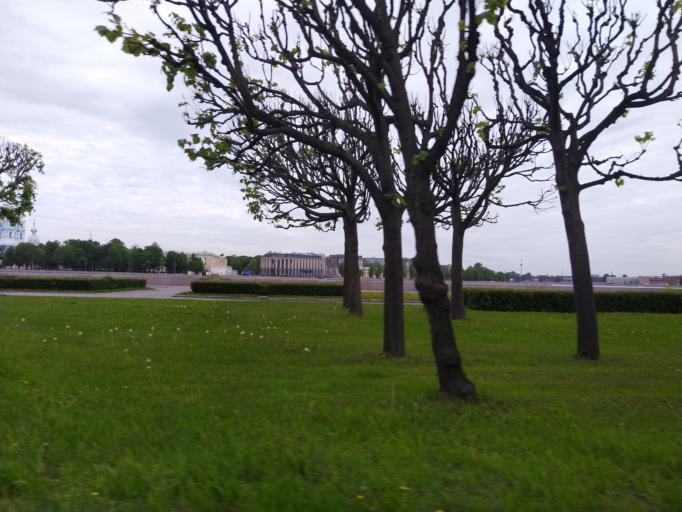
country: RU
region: Leningrad
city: Finlyandskiy
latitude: 59.9519
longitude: 30.4070
